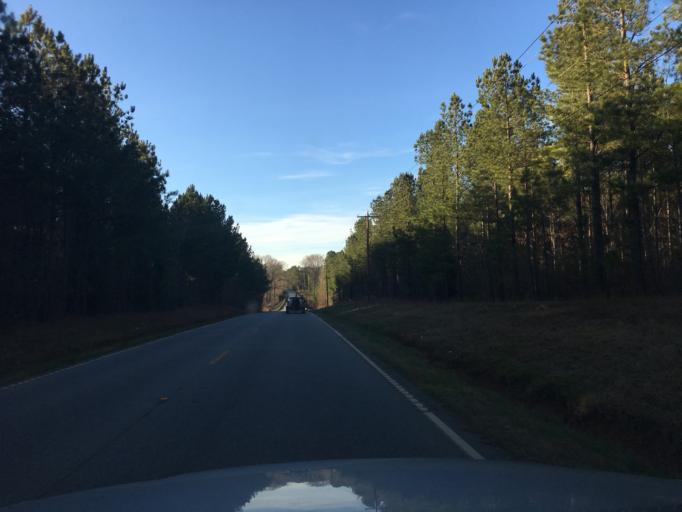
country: US
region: South Carolina
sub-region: Saluda County
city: Saluda
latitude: 34.0340
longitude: -81.8051
